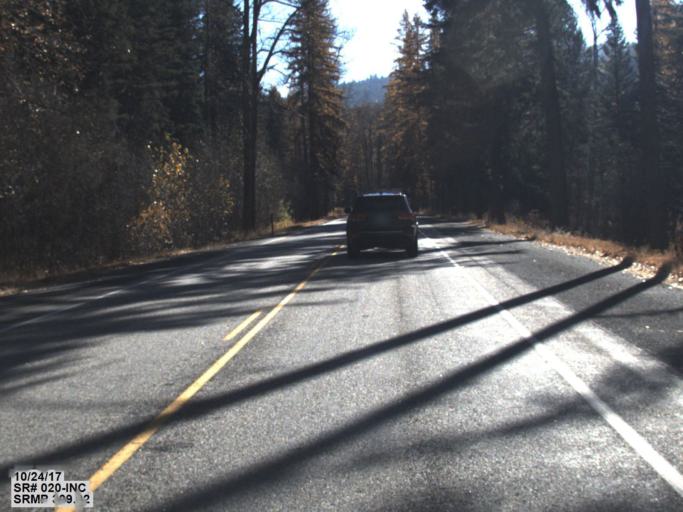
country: US
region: Washington
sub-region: Ferry County
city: Republic
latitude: 48.6017
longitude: -118.6542
